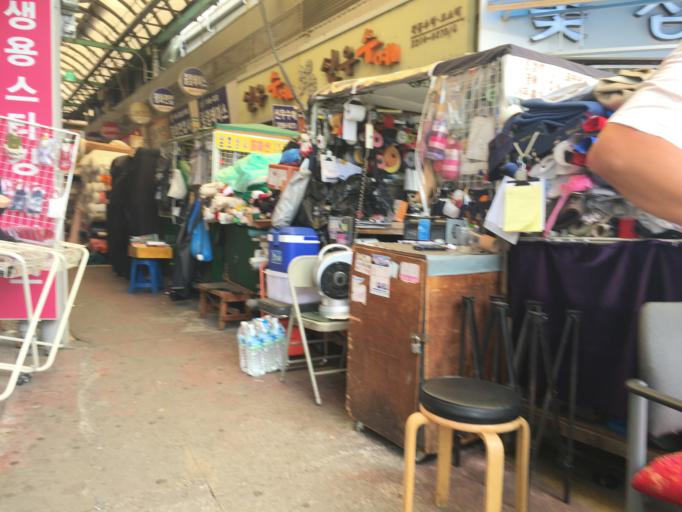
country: KR
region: Seoul
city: Seoul
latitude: 37.5694
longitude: 127.0003
